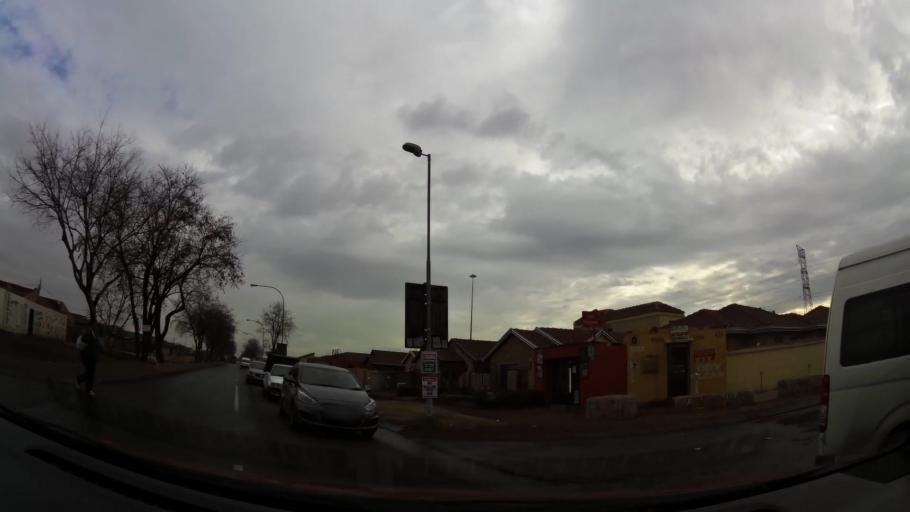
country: ZA
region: Gauteng
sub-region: City of Johannesburg Metropolitan Municipality
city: Soweto
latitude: -26.2849
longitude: 27.8485
